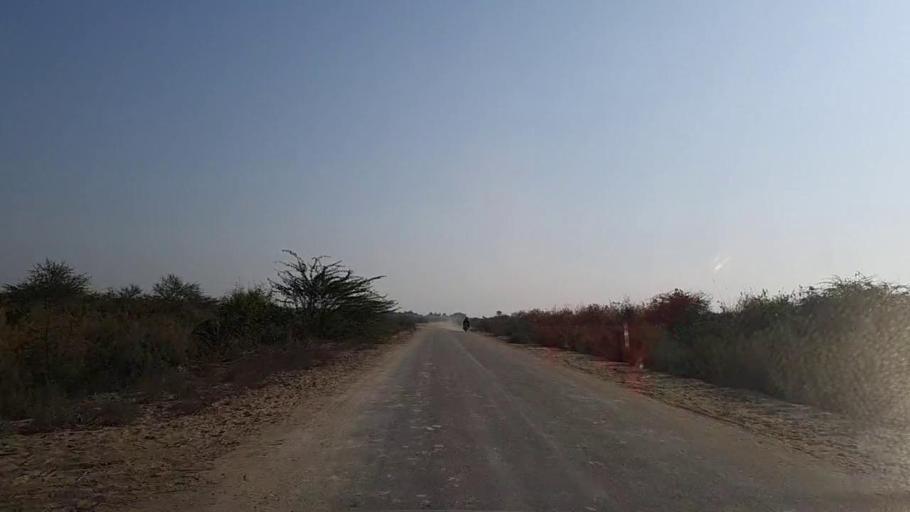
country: PK
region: Sindh
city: Tando Mittha Khan
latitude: 25.9092
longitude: 69.0763
